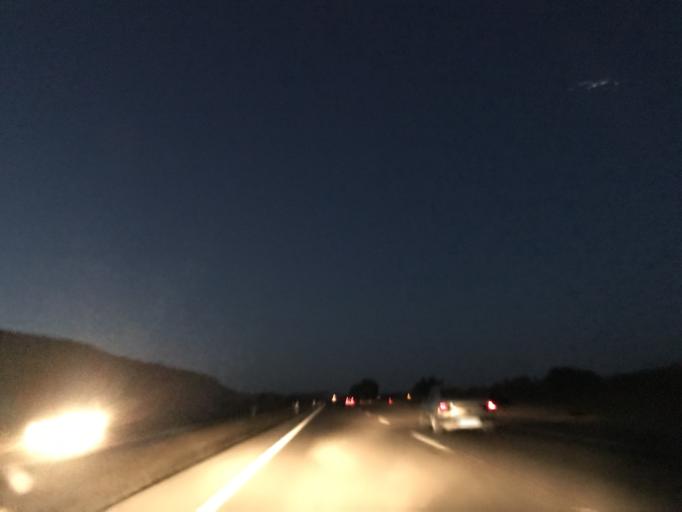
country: TR
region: Yozgat
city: Yerkoy
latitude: 39.6682
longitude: 34.5713
